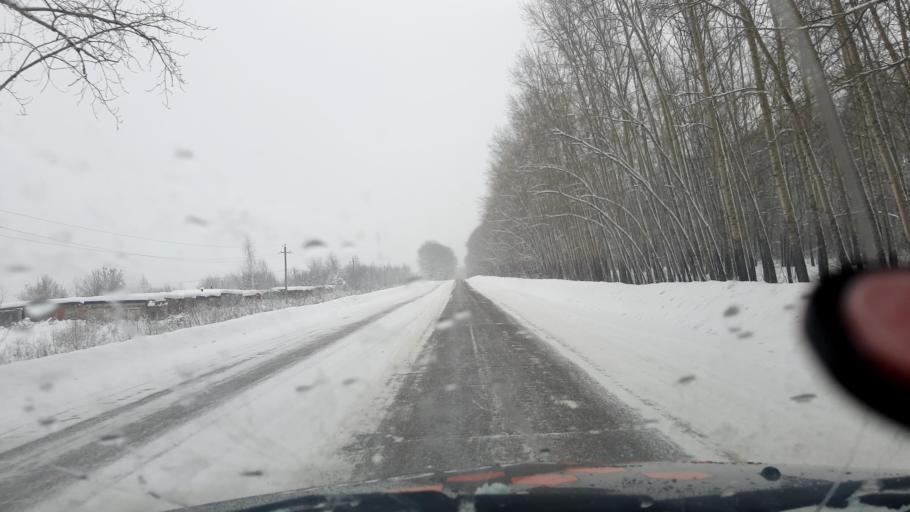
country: RU
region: Bashkortostan
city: Blagoveshchensk
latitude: 55.0370
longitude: 56.0096
